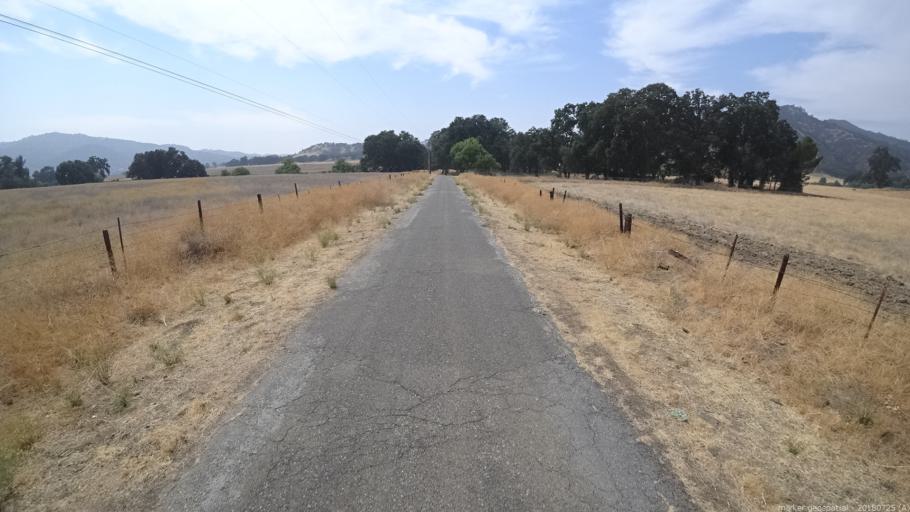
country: US
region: California
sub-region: Fresno County
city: Coalinga
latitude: 36.2128
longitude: -120.7024
